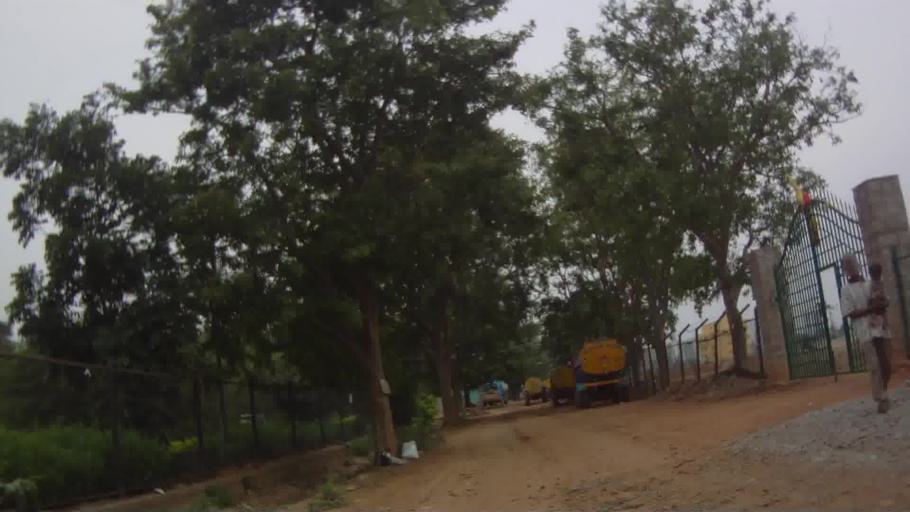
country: IN
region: Karnataka
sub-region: Bangalore Urban
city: Bangalore
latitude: 12.9621
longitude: 77.7090
